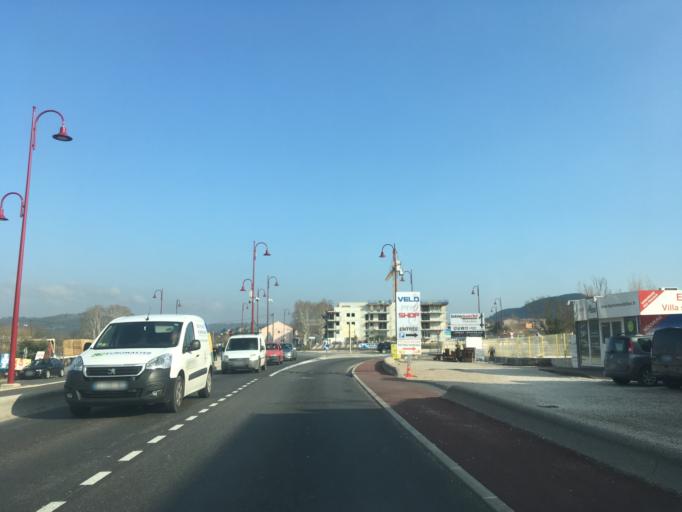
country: FR
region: Provence-Alpes-Cote d'Azur
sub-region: Departement du Var
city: Vidauban
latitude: 43.4218
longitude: 6.4261
